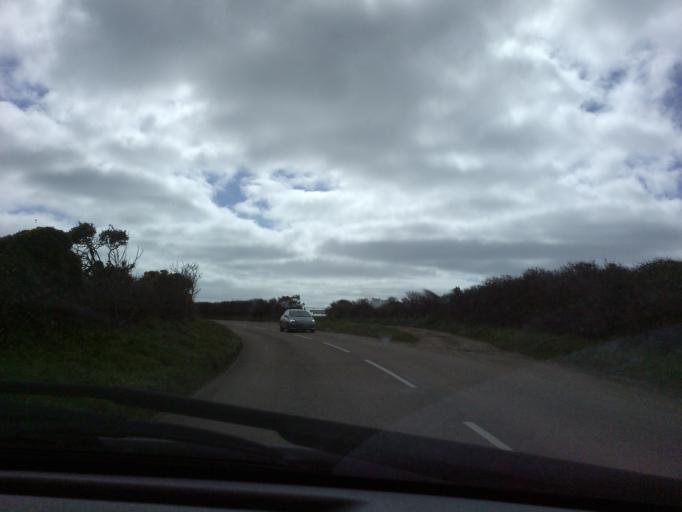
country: GB
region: England
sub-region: Cornwall
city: St. Buryan
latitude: 50.0584
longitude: -5.6371
